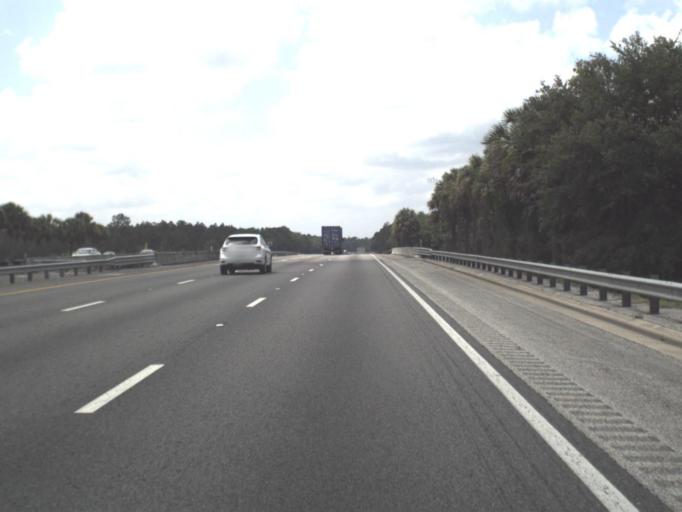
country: US
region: Florida
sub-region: Flagler County
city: Palm Coast
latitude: 29.6718
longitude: -81.3040
